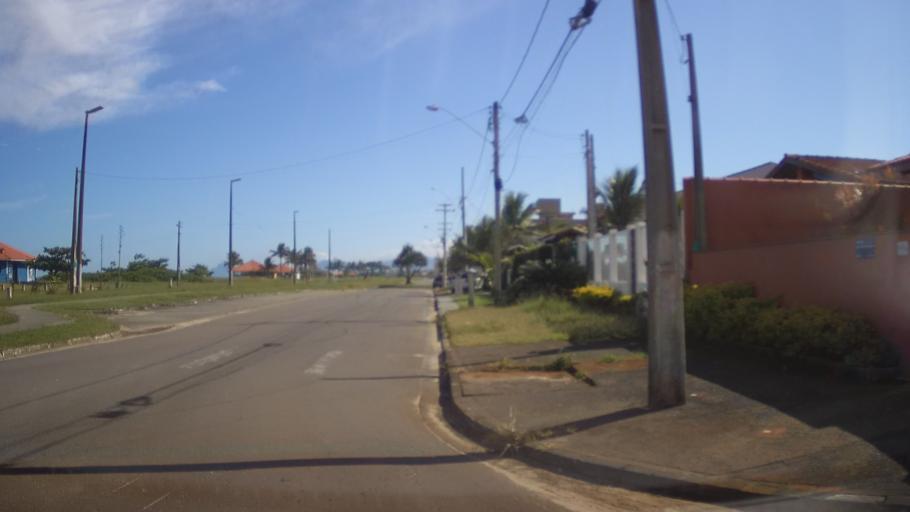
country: BR
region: Sao Paulo
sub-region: Itanhaem
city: Itanhaem
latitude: -24.2081
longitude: -46.8306
